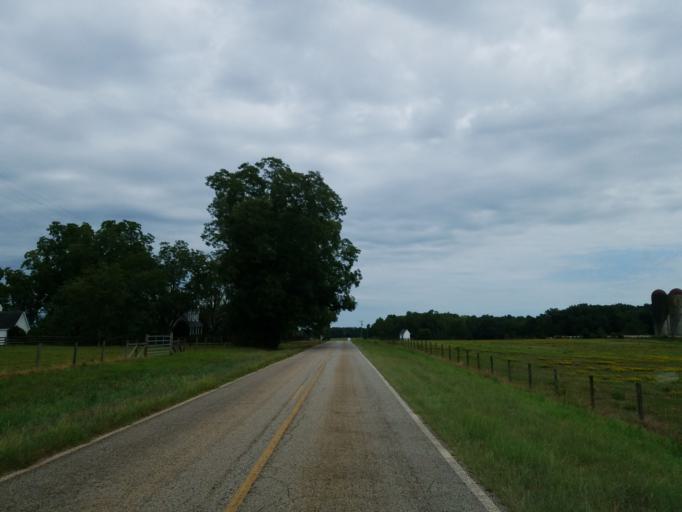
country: US
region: Georgia
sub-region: Lamar County
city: Barnesville
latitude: 32.9984
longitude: -84.0535
